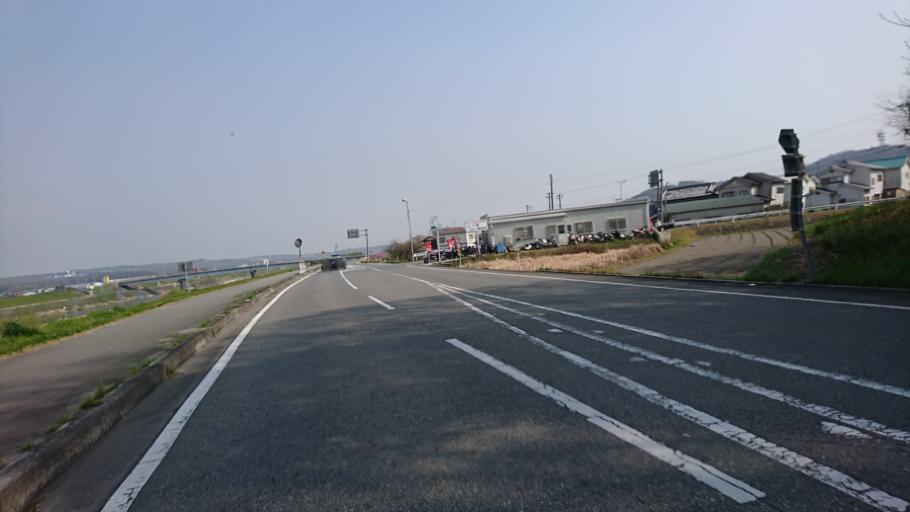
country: JP
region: Hyogo
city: Ono
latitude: 34.8389
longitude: 134.9157
